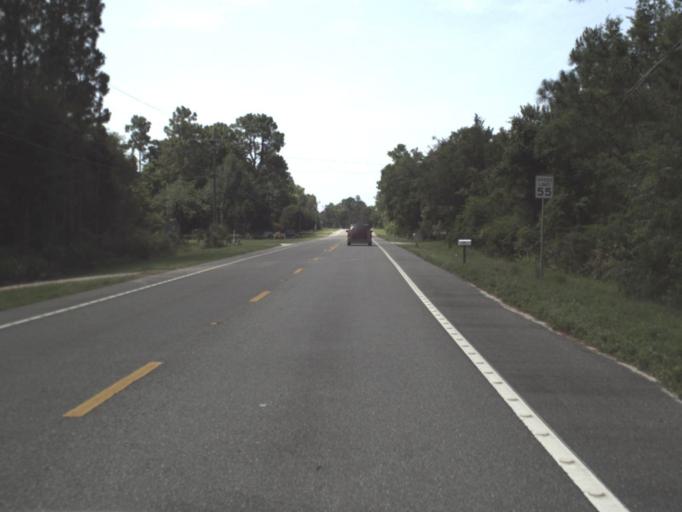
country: US
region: Florida
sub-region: Taylor County
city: Steinhatchee
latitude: 29.6959
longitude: -83.3568
